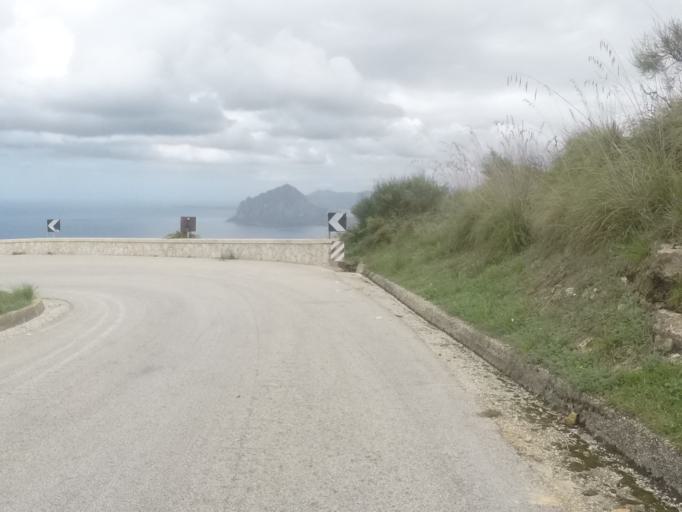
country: IT
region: Sicily
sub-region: Trapani
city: Erice
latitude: 38.0484
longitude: 12.5810
